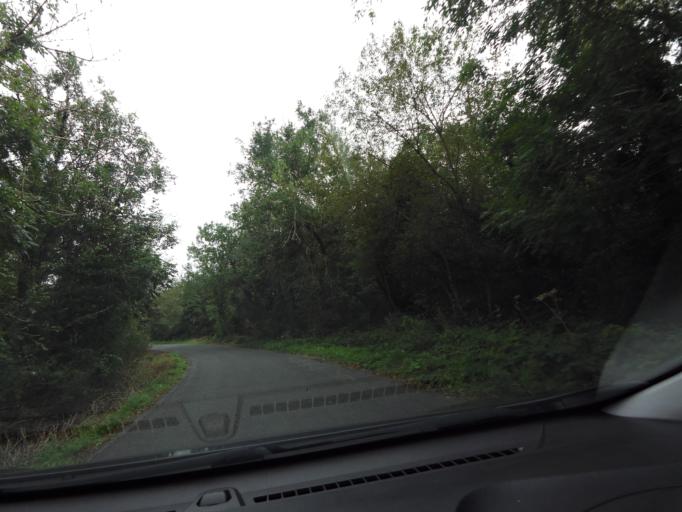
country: IE
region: Connaught
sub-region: County Galway
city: Loughrea
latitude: 53.2888
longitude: -8.5909
